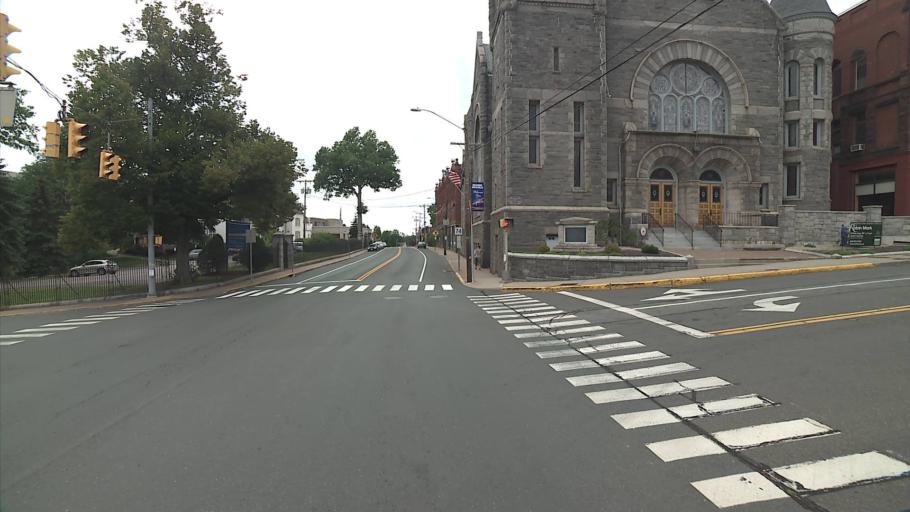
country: US
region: Connecticut
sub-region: Tolland County
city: Rockville
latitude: 41.8670
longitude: -72.4494
